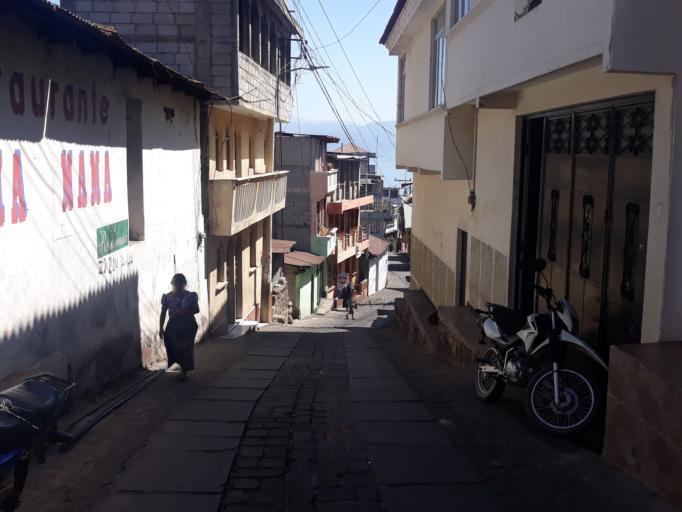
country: GT
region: Solola
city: San Pedro La Laguna
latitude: 14.6922
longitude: -91.2717
